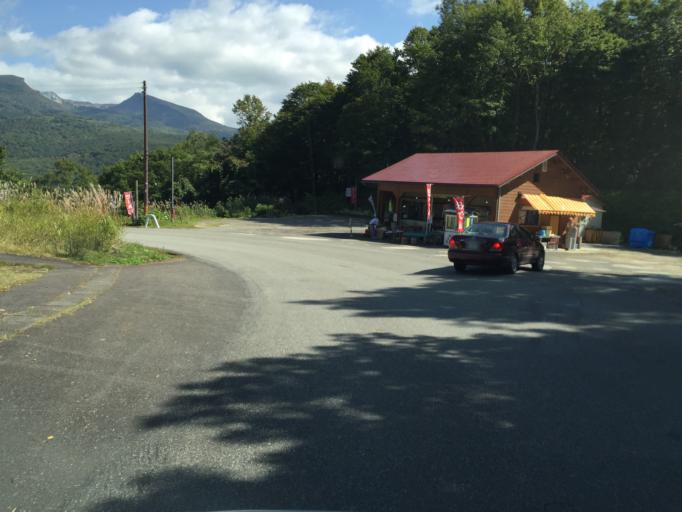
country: JP
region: Fukushima
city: Inawashiro
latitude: 37.6477
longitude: 140.2159
